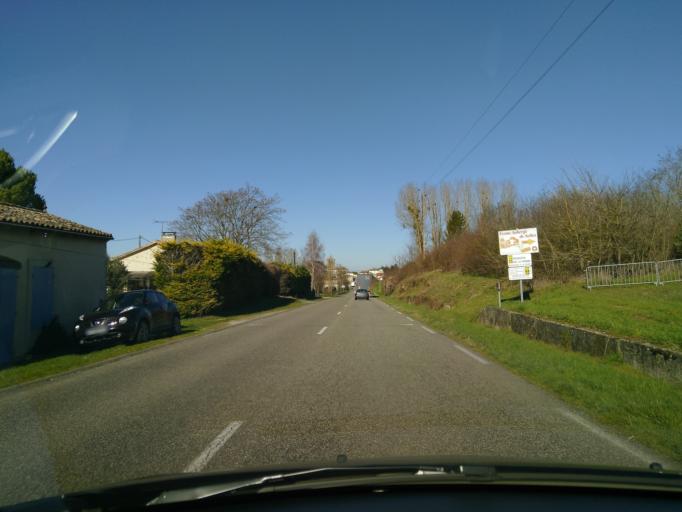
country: FR
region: Aquitaine
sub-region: Departement du Lot-et-Garonne
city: Cancon
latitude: 44.5779
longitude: 0.6250
